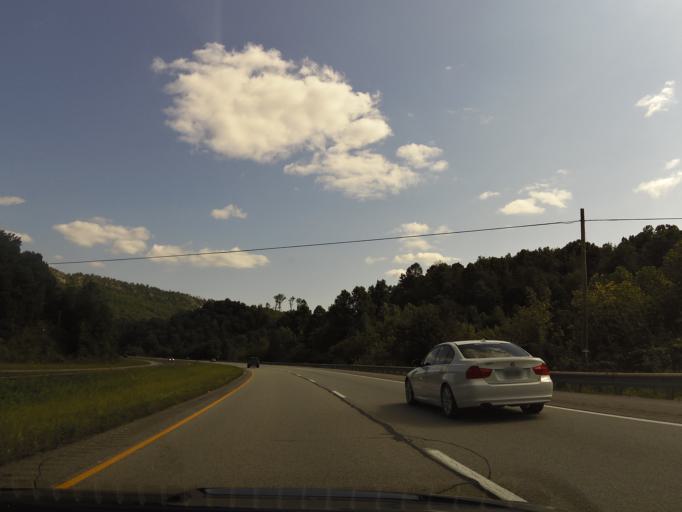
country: US
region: Kentucky
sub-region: Bell County
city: Pineville
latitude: 36.6994
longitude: -83.6930
